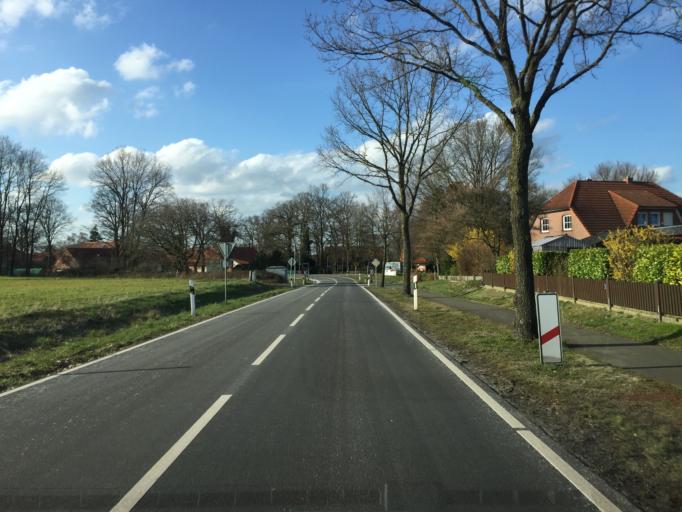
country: DE
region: Lower Saxony
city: Varrel
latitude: 52.6535
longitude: 8.7501
